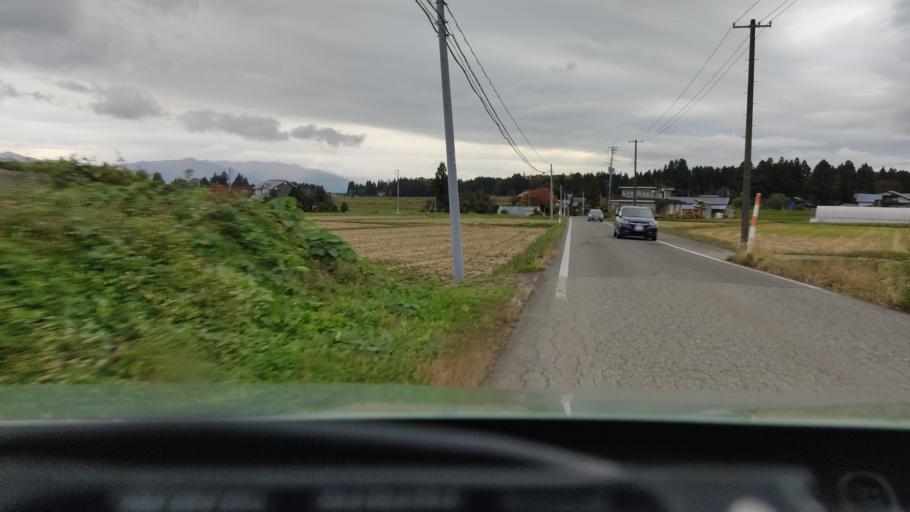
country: JP
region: Akita
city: Kakunodatemachi
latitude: 39.5663
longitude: 140.6113
